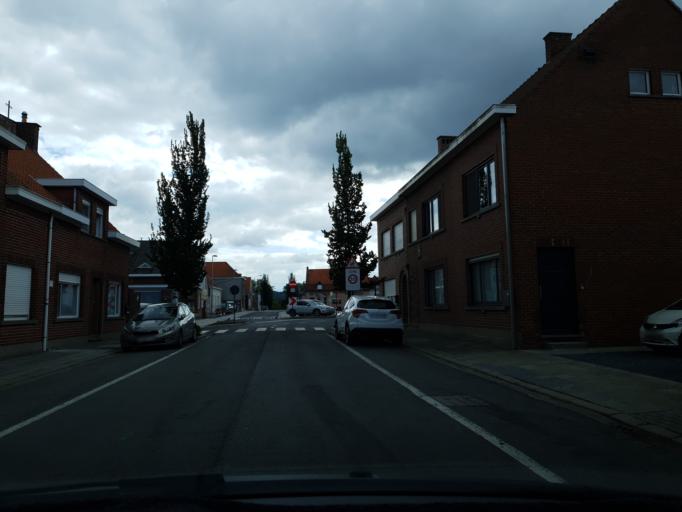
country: BE
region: Flanders
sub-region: Provincie West-Vlaanderen
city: Avelgem
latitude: 50.7805
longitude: 3.4646
